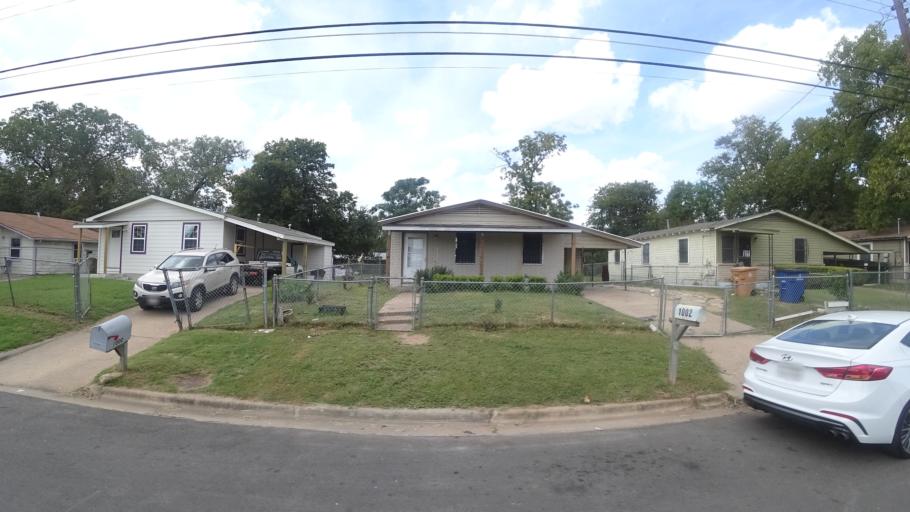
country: US
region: Texas
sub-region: Travis County
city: Austin
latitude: 30.2624
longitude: -97.6999
